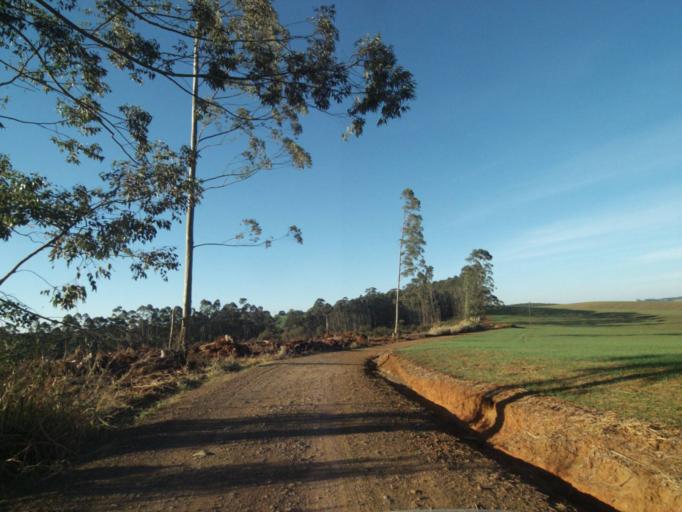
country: BR
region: Parana
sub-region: Telemaco Borba
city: Telemaco Borba
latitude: -24.4809
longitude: -50.5930
